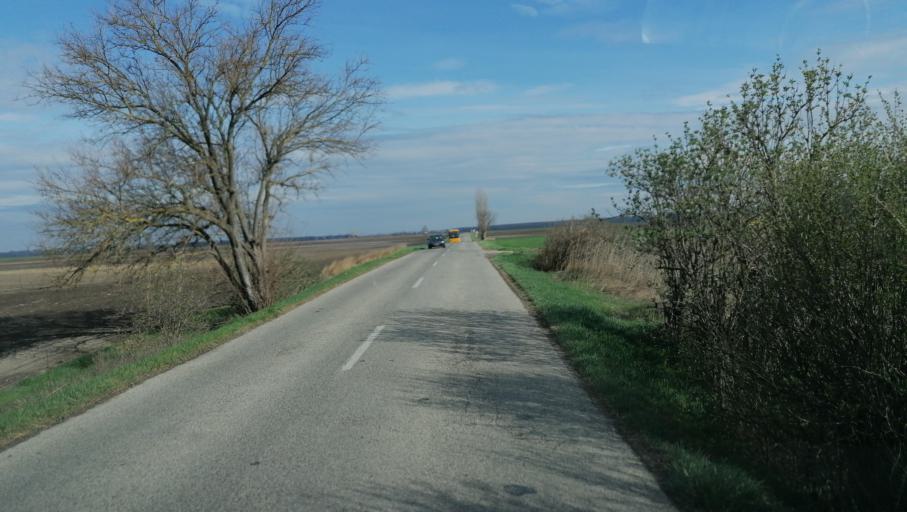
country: HU
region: Pest
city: Rackeve
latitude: 47.1013
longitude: 18.9270
